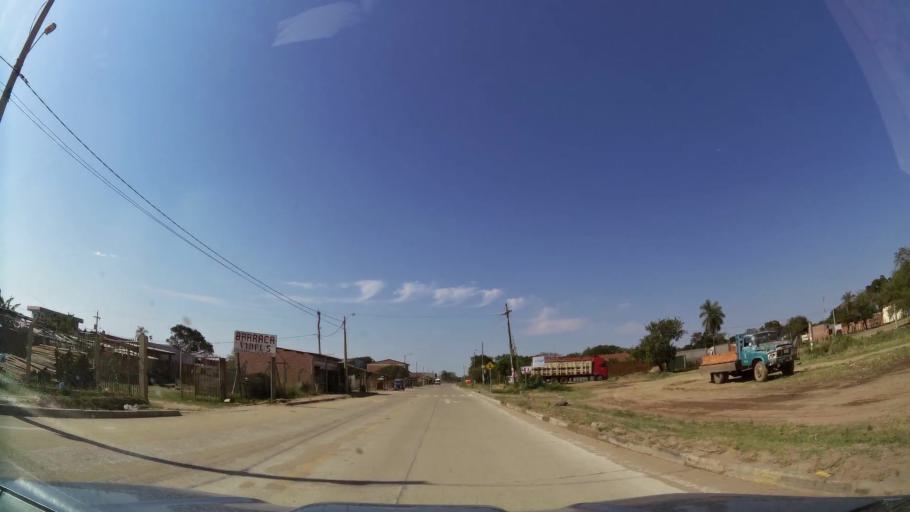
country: BO
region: Santa Cruz
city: Cotoca
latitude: -17.7264
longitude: -63.0865
